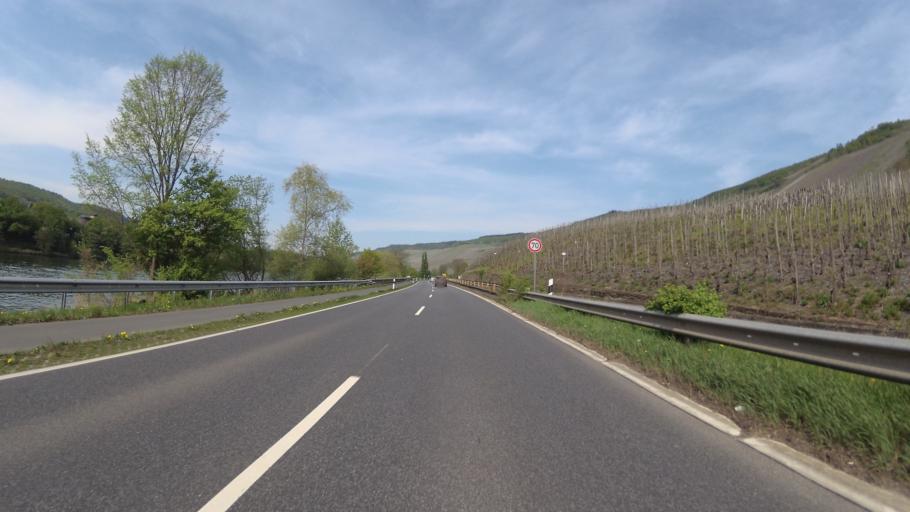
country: DE
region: Rheinland-Pfalz
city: Bernkastel-Kues
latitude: 49.9303
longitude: 7.0661
